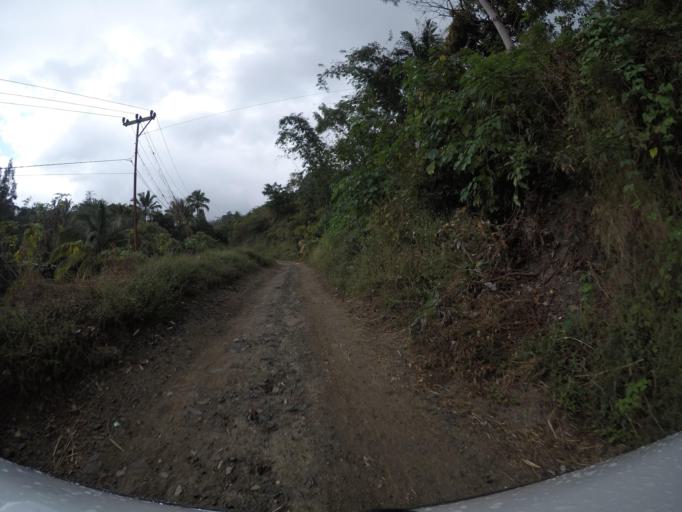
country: TL
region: Baucau
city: Baucau
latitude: -8.6391
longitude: 126.6430
